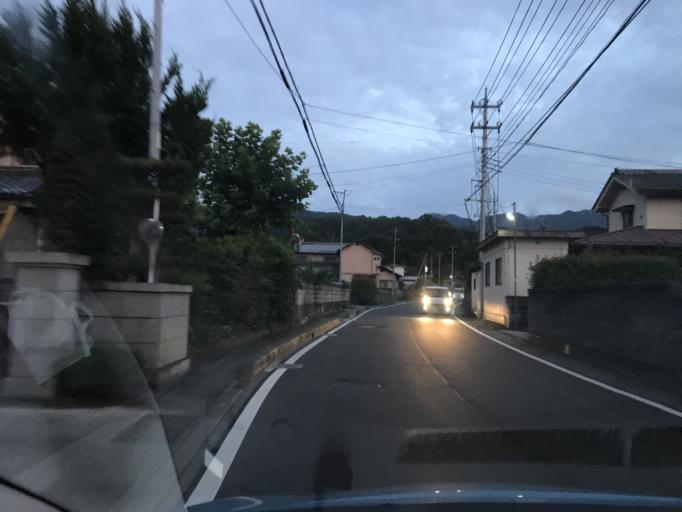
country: JP
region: Yamanashi
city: Ryuo
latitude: 35.5809
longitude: 138.5484
